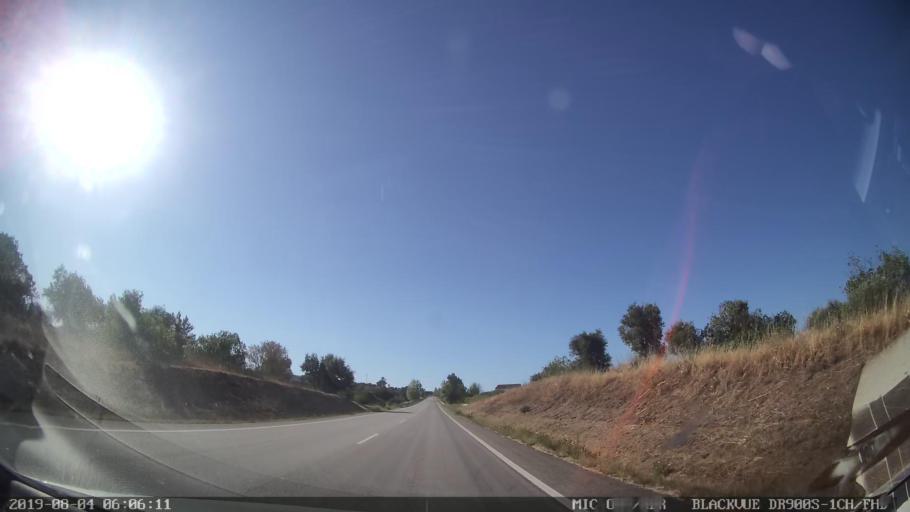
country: PT
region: Santarem
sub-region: Abrantes
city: Alferrarede
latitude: 39.4787
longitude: -8.0850
